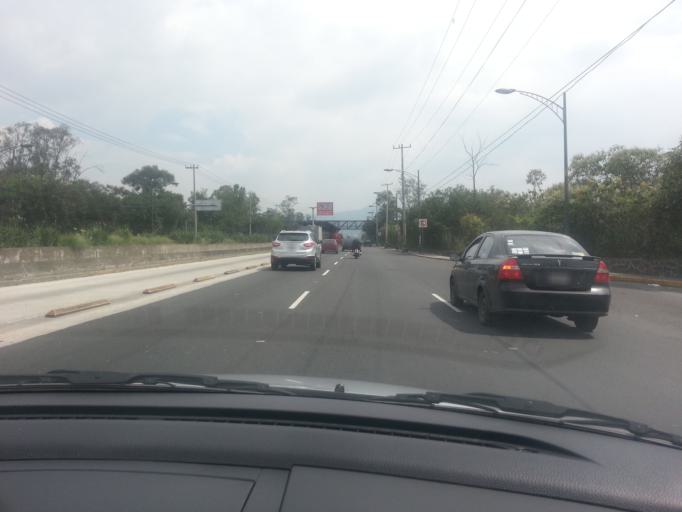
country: MX
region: Mexico City
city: Tlalpan
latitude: 19.3167
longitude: -99.1878
